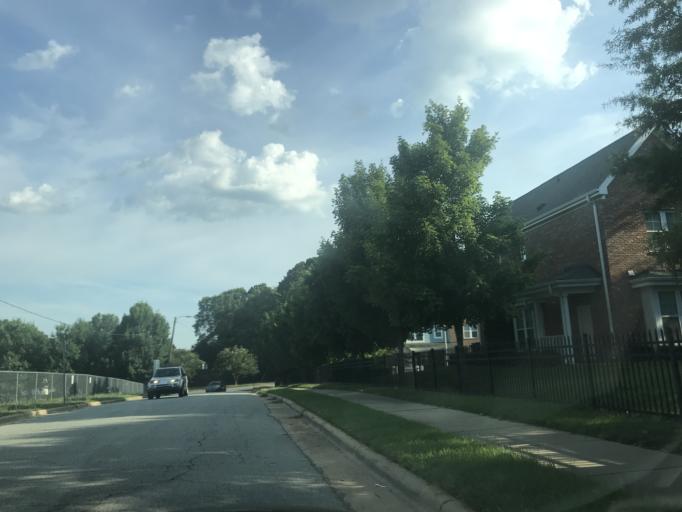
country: US
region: North Carolina
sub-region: Wake County
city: Raleigh
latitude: 35.7688
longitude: -78.6271
